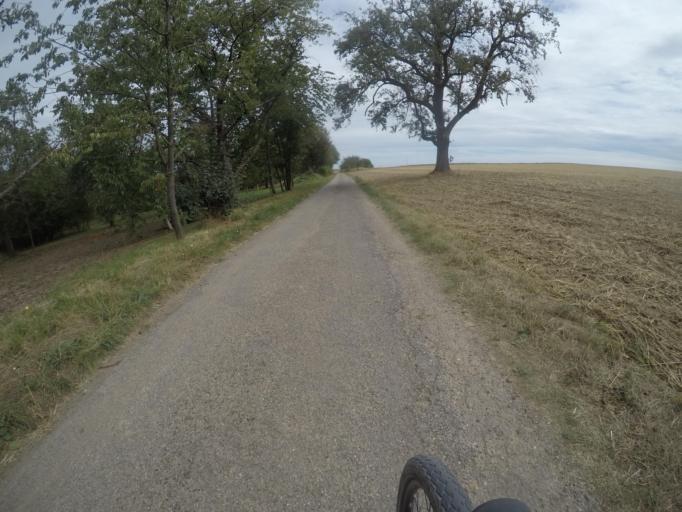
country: DE
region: Baden-Wuerttemberg
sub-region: Karlsruhe Region
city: Muhlacker
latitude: 48.9346
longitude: 8.8133
